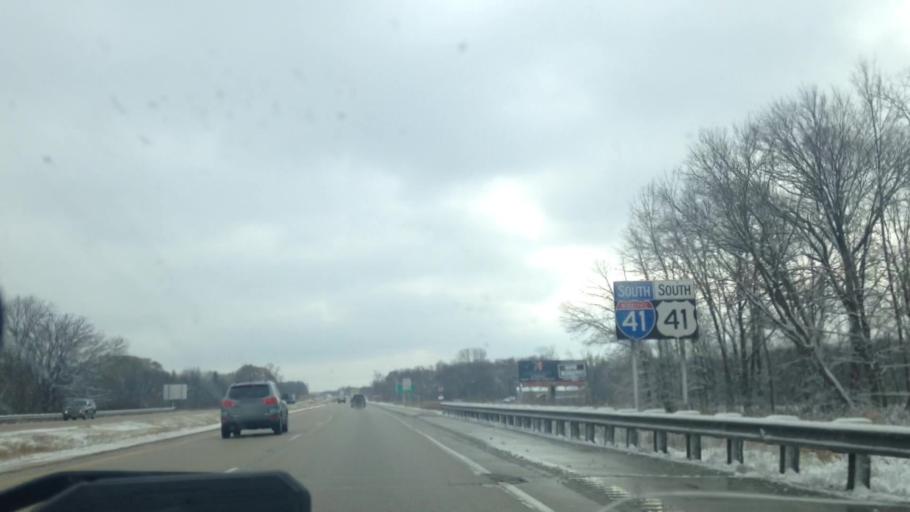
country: US
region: Wisconsin
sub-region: Washington County
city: Slinger
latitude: 43.4169
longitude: -88.3316
